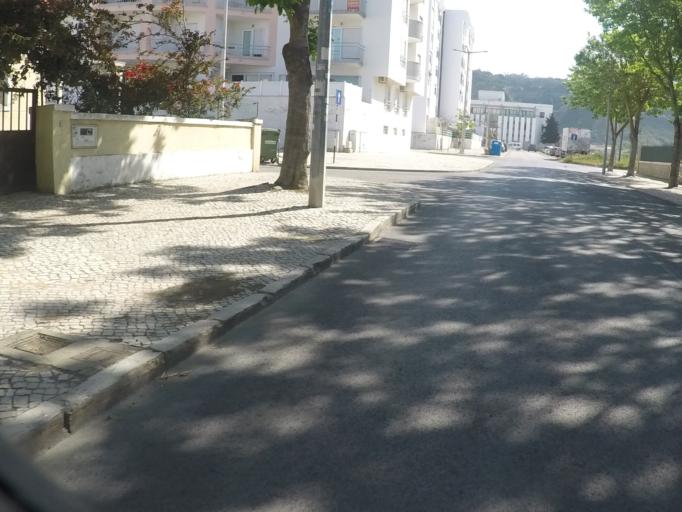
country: PT
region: Setubal
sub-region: Almada
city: Costa de Caparica
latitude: 38.6418
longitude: -9.2312
